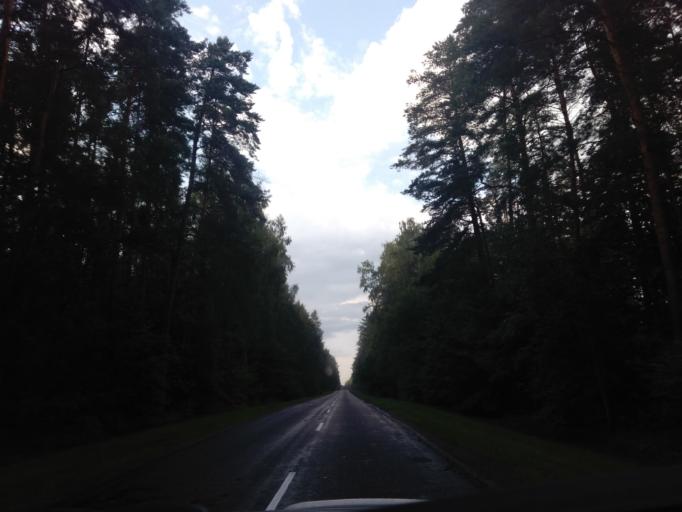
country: BY
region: Minsk
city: Uzda
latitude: 53.3678
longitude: 27.1029
